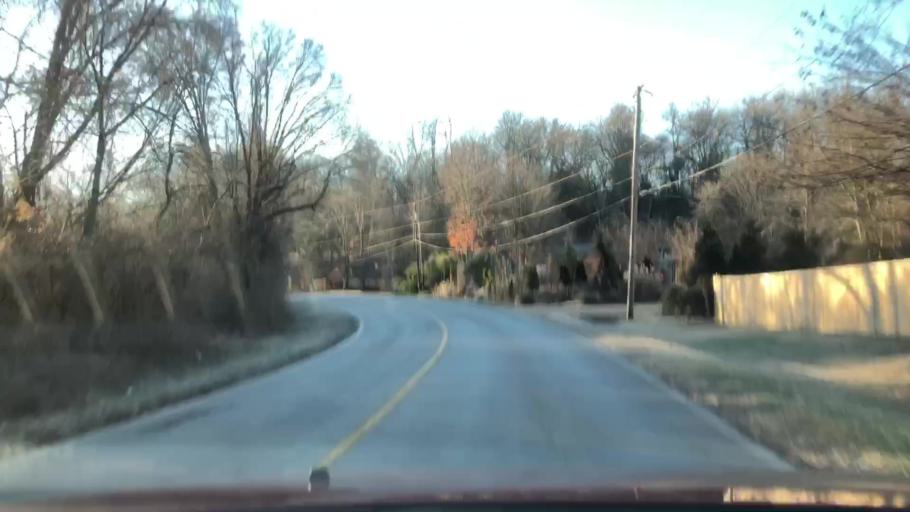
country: US
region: Missouri
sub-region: Greene County
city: Springfield
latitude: 37.1628
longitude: -93.2448
